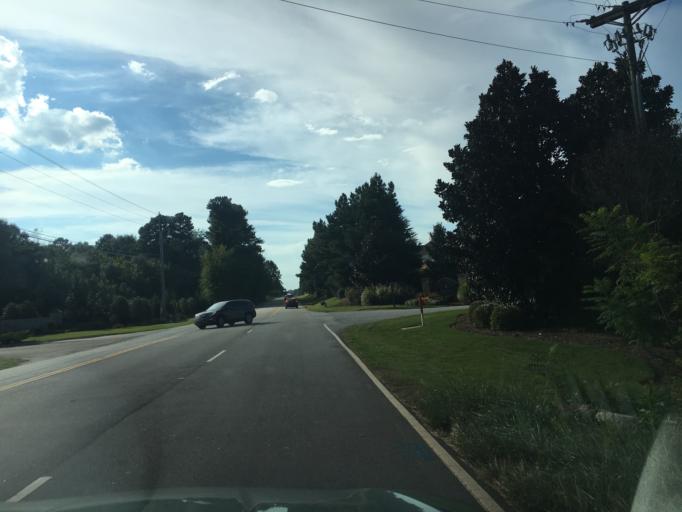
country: US
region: South Carolina
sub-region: Greenville County
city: Five Forks
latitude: 34.8028
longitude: -82.2095
